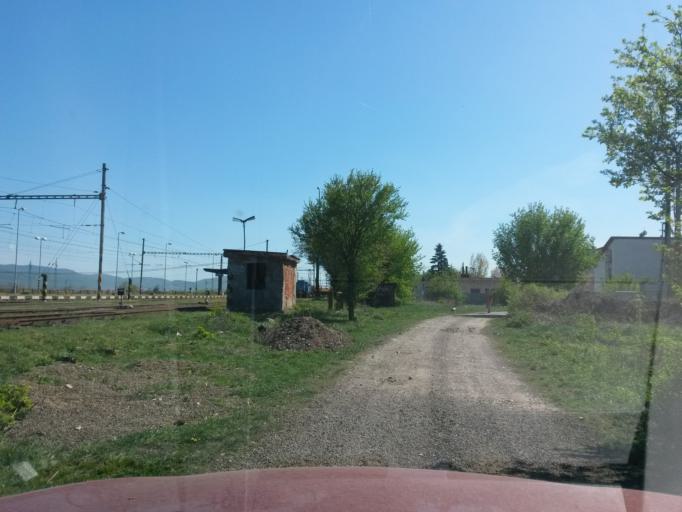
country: SK
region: Kosicky
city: Kosice
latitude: 48.6802
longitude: 21.2755
